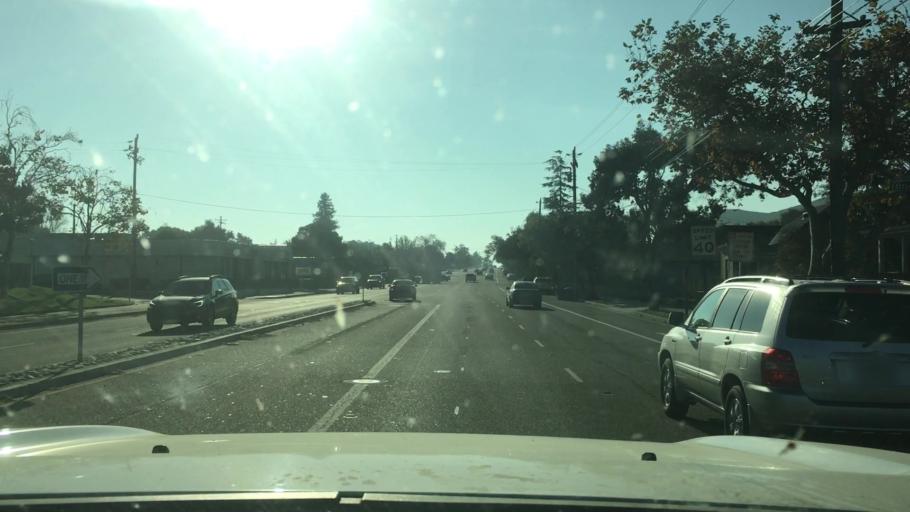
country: US
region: California
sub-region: San Luis Obispo County
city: San Luis Obispo
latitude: 35.2685
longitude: -120.6556
